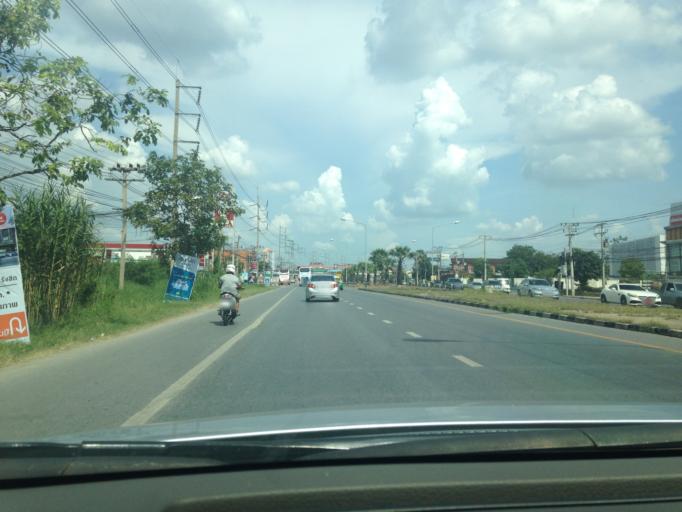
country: TH
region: Phra Nakhon Si Ayutthaya
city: Ban Bang Kadi Pathum Thani
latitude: 14.0056
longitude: 100.5591
